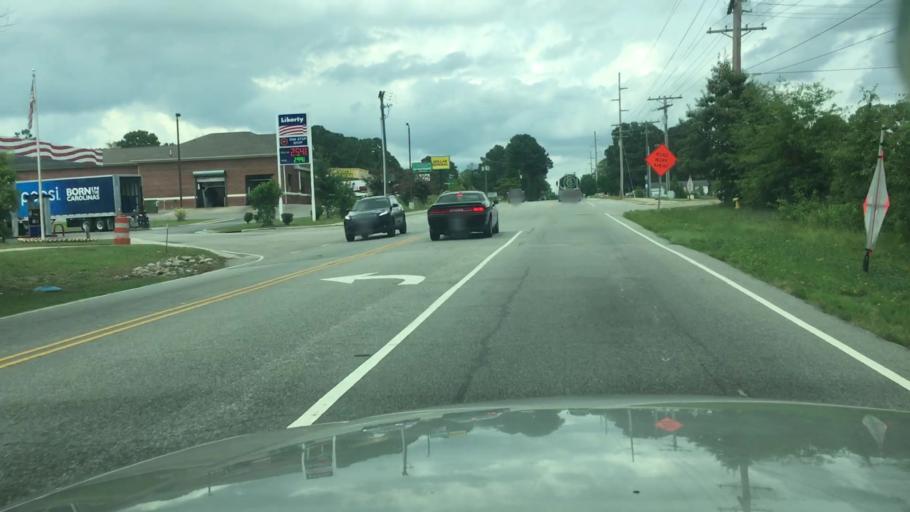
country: US
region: North Carolina
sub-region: Hoke County
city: Rockfish
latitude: 35.0145
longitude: -79.0095
